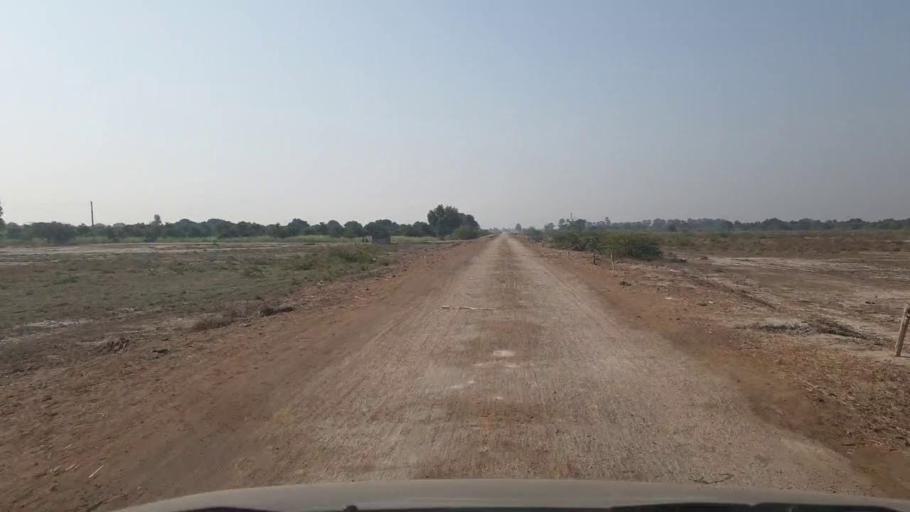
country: PK
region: Sindh
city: Mirwah Gorchani
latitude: 25.2720
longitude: 69.1188
